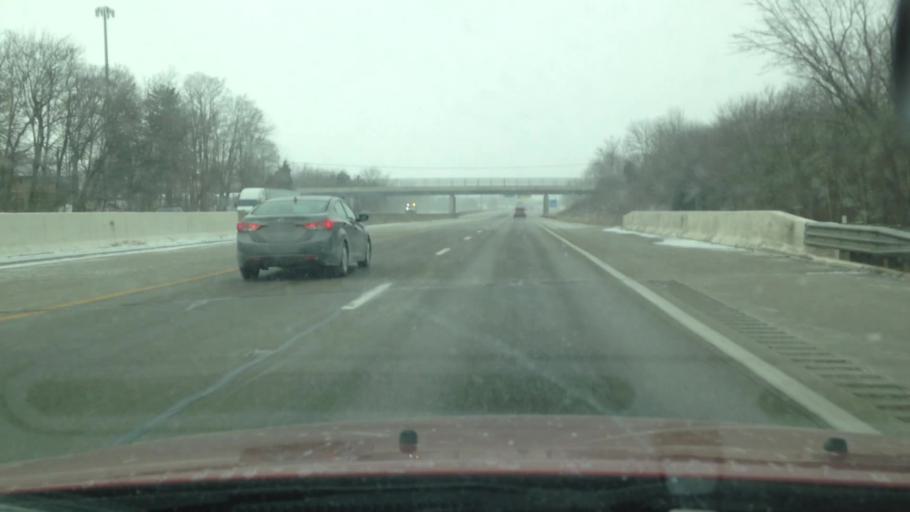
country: US
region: Ohio
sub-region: Montgomery County
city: Clayton
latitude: 39.8543
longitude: -84.3565
